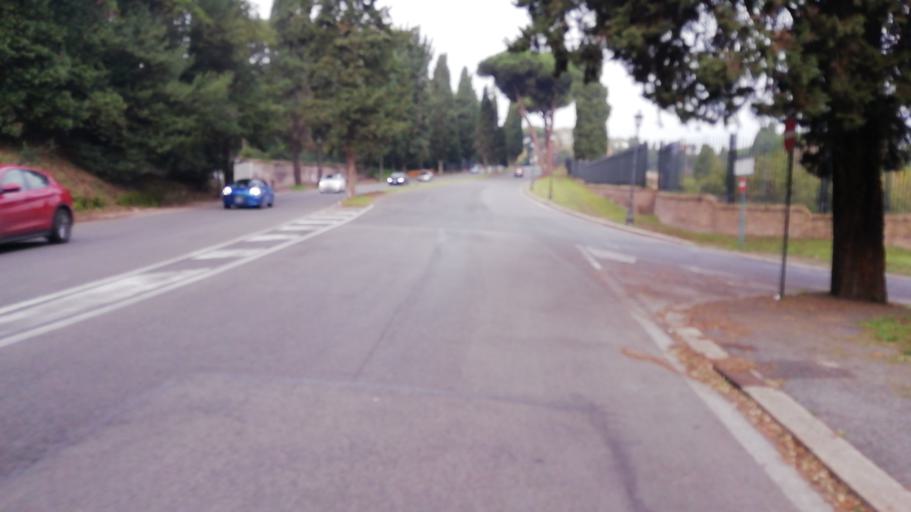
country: IT
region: Latium
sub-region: Citta metropolitana di Roma Capitale
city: Rome
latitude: 41.8767
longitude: 12.4929
